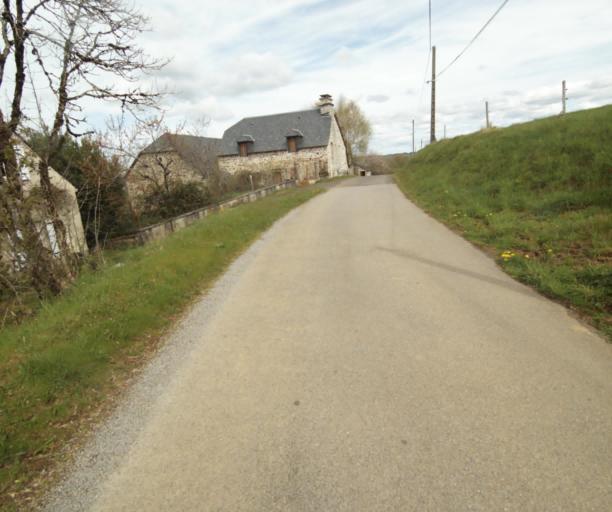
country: FR
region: Limousin
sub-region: Departement de la Correze
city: Laguenne
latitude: 45.2240
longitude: 1.8473
